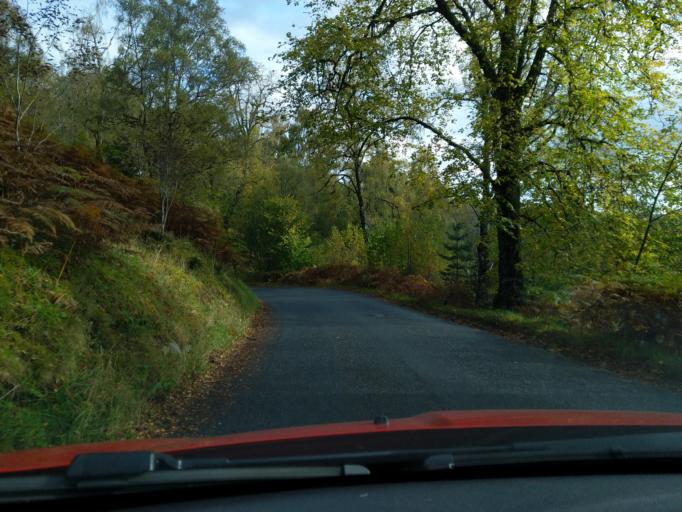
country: GB
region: Scotland
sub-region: Perth and Kinross
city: Aberfeldy
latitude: 56.7072
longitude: -4.0856
